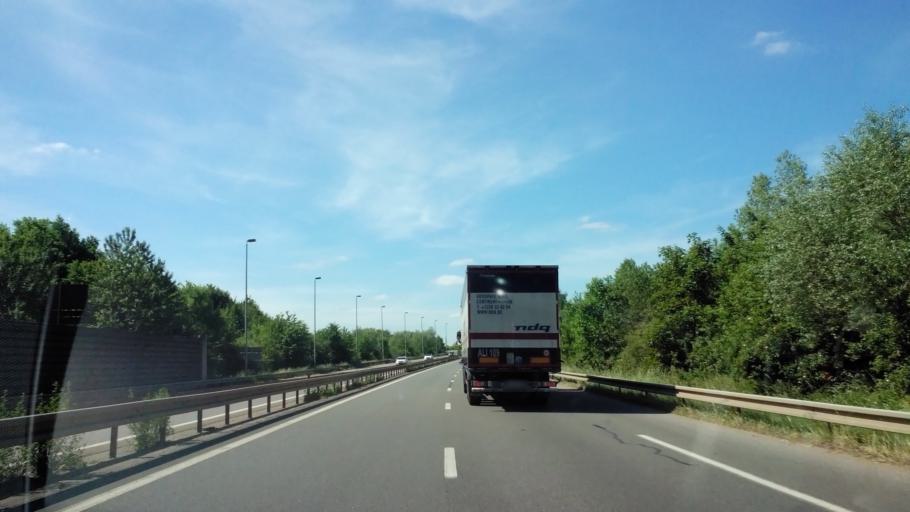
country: FR
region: Lorraine
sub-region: Departement de la Moselle
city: Peltre
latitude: 49.0984
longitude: 6.2348
